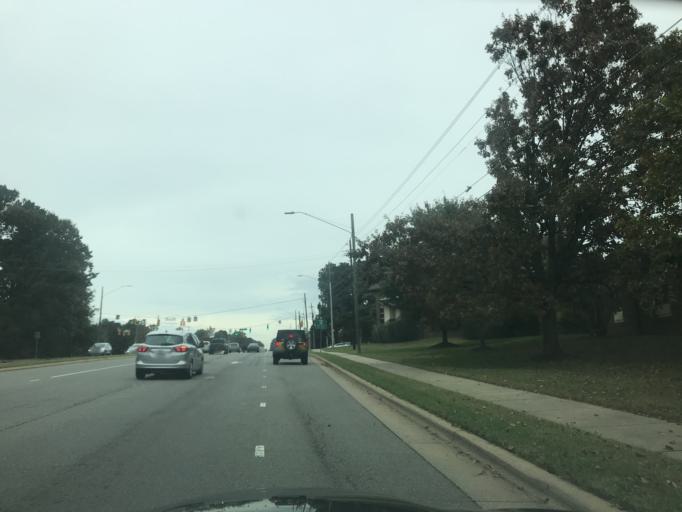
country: US
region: North Carolina
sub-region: Wake County
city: West Raleigh
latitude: 35.8817
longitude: -78.6789
